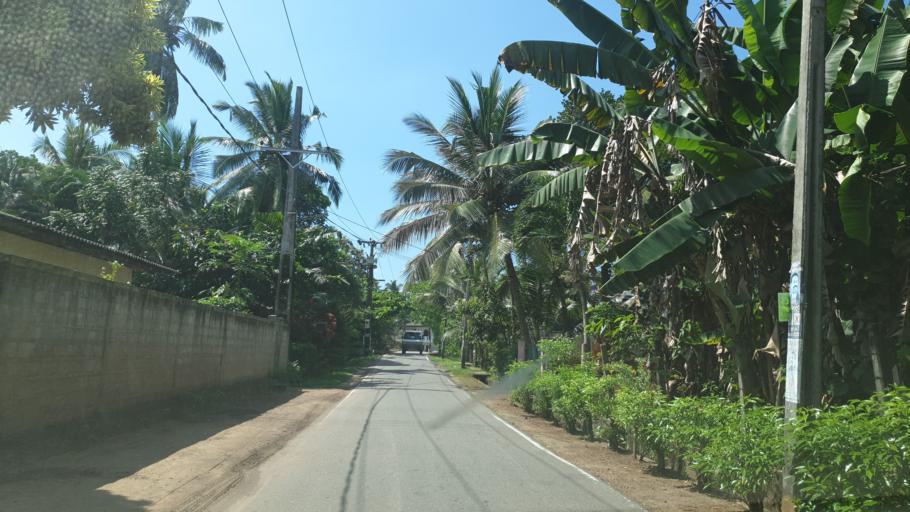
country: LK
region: Western
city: Panadura
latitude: 6.6835
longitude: 79.9302
